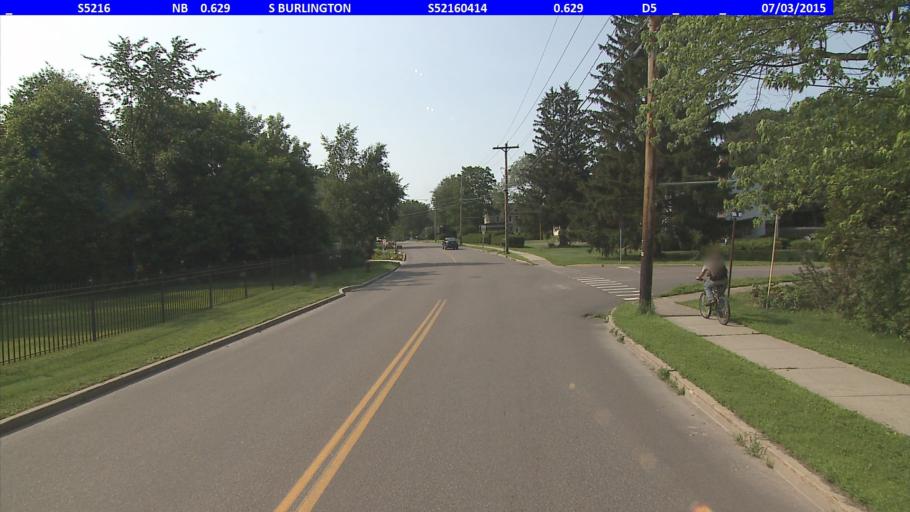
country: US
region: Vermont
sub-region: Chittenden County
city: South Burlington
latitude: 44.4758
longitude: -73.1736
